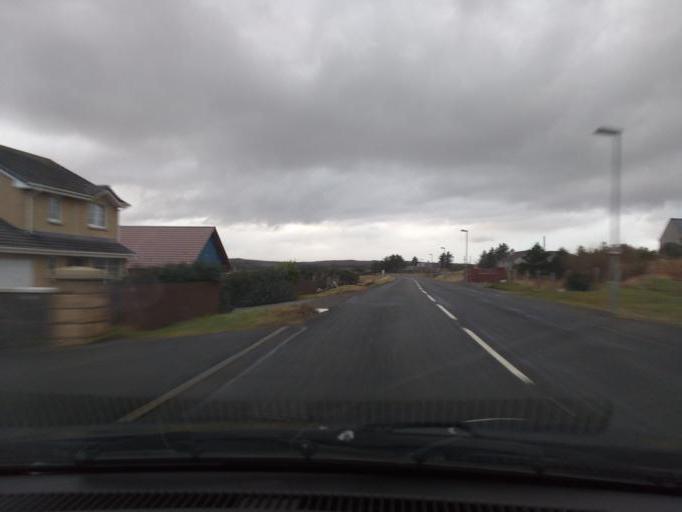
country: GB
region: Scotland
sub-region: Eilean Siar
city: Isle of Lewis
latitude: 58.2428
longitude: -6.3554
